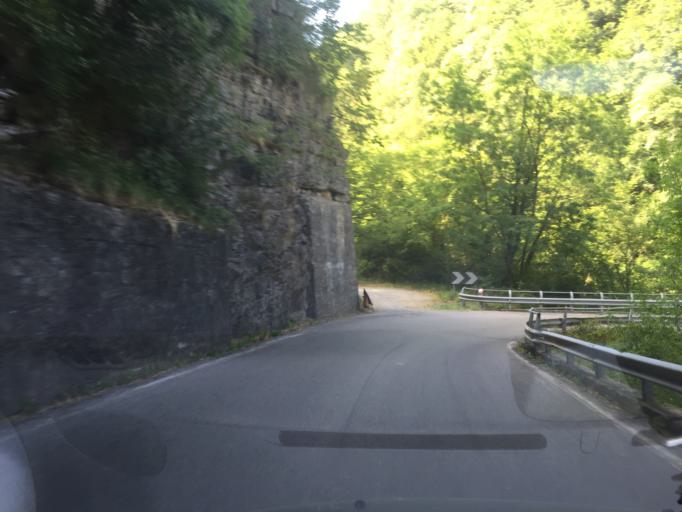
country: IT
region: Tuscany
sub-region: Provincia di Lucca
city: Careggine
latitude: 44.1329
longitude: 10.3053
